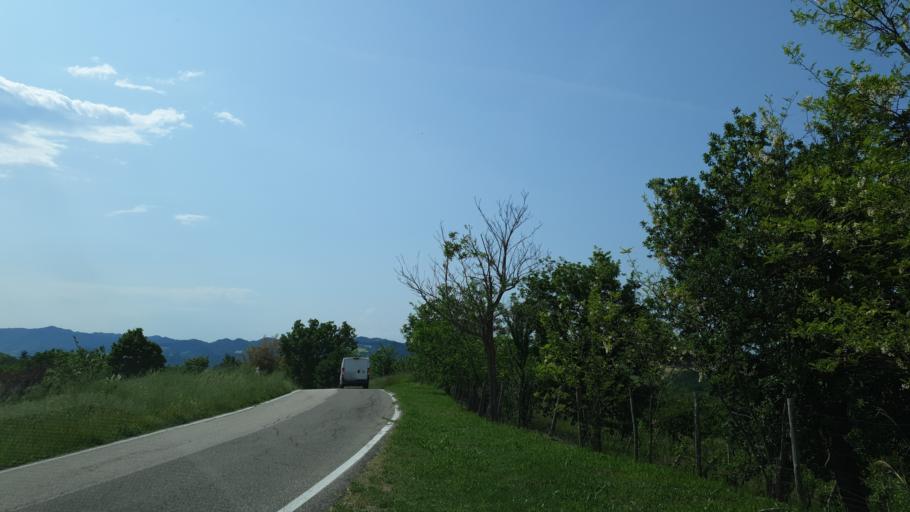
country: IT
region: Emilia-Romagna
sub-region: Provincia di Rimini
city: Sant'Agata Feltria
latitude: 43.9112
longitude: 12.2096
